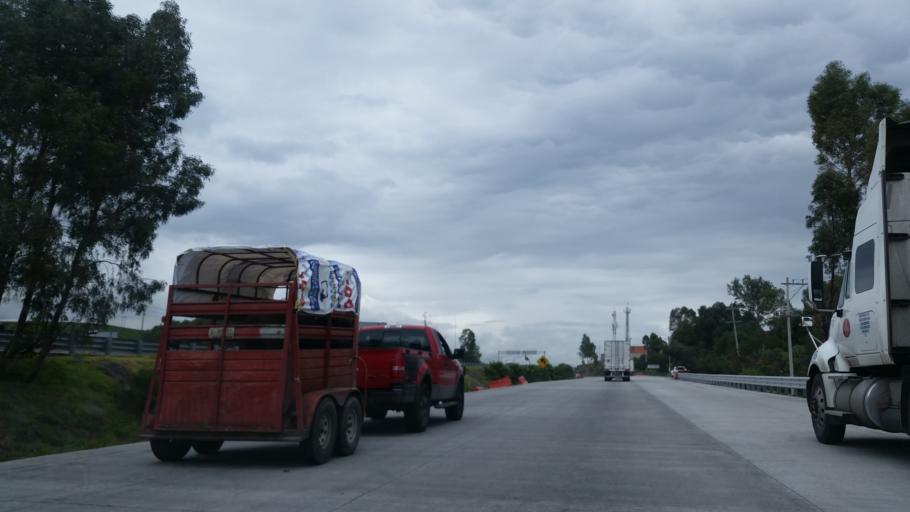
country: MX
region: Hidalgo
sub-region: Tepeji del Rio de Ocampo
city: Cantera de Villagran
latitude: 19.8508
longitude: -99.2858
